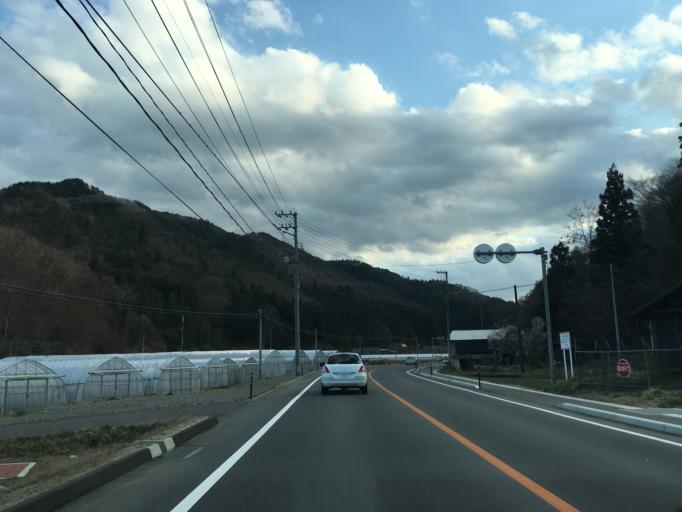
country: JP
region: Fukushima
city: Ishikawa
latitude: 37.0915
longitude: 140.5282
